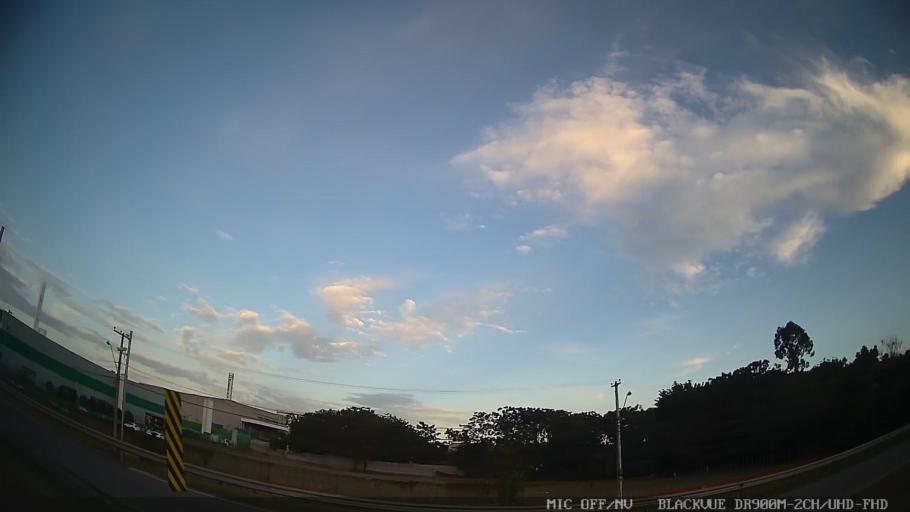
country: BR
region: Sao Paulo
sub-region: Indaiatuba
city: Indaiatuba
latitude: -23.1363
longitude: -47.2399
